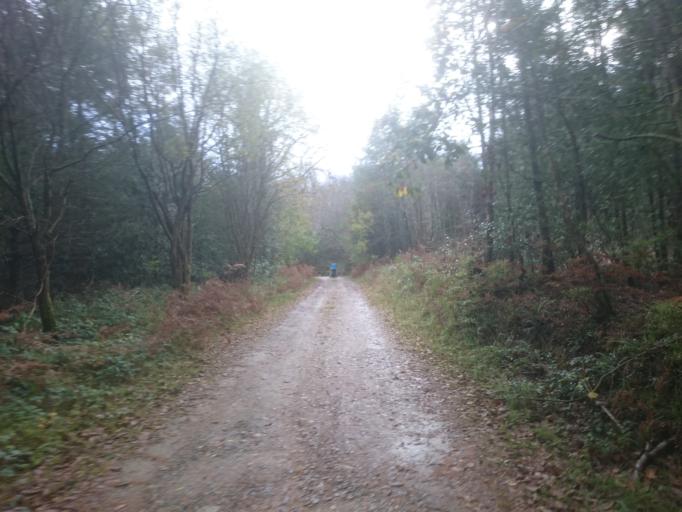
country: IE
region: Leinster
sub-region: Kilkenny
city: Thomastown
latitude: 52.4687
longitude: -7.0521
